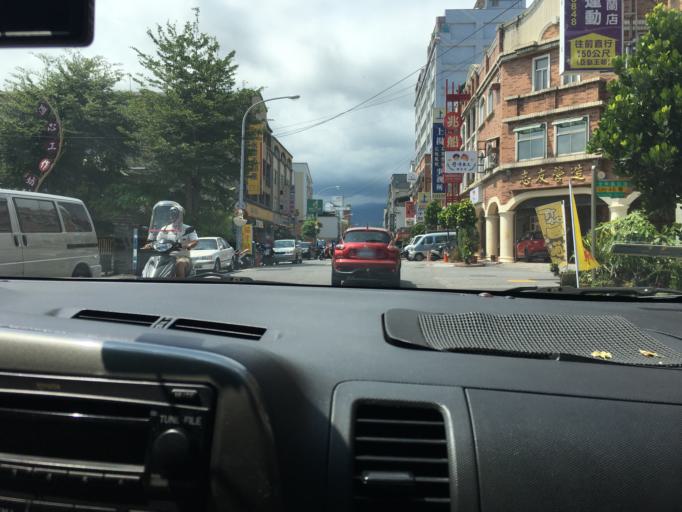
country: TW
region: Taiwan
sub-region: Yilan
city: Yilan
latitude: 24.7459
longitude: 121.7413
